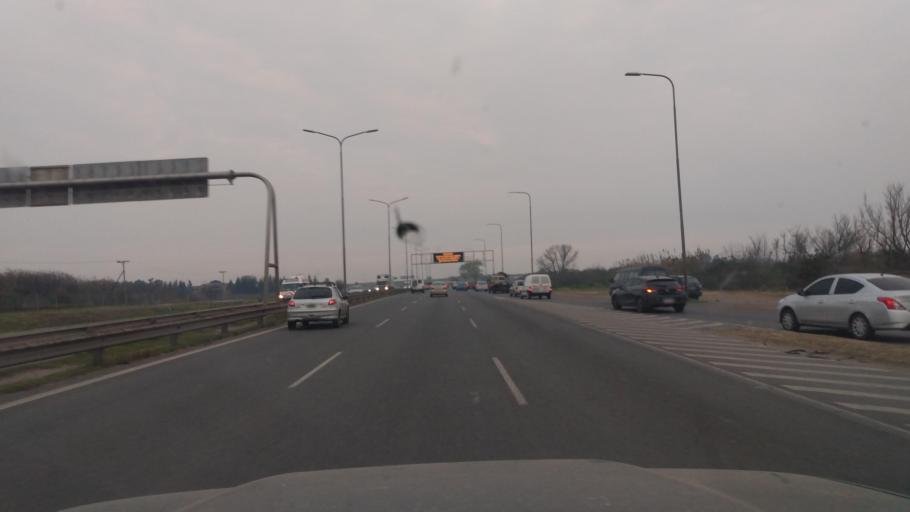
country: AR
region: Buenos Aires
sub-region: Partido de Tigre
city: Tigre
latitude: -34.4906
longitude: -58.5962
